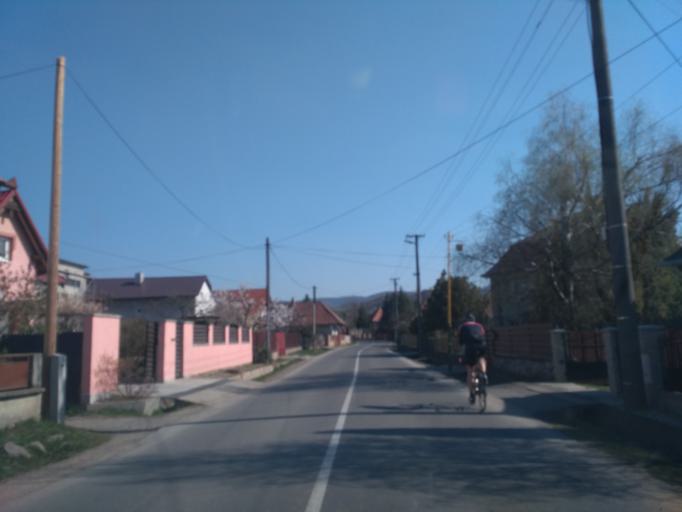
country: SK
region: Kosicky
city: Kosice
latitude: 48.6001
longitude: 21.3477
